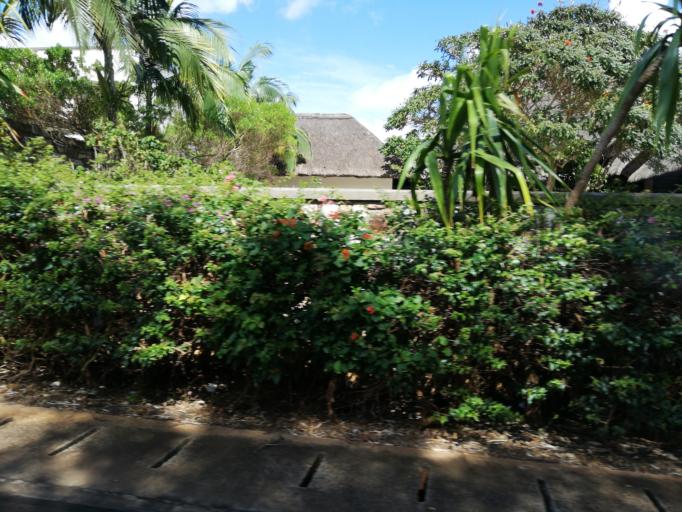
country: MU
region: Pamplemousses
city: Arsenal
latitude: -20.1000
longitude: 57.5141
